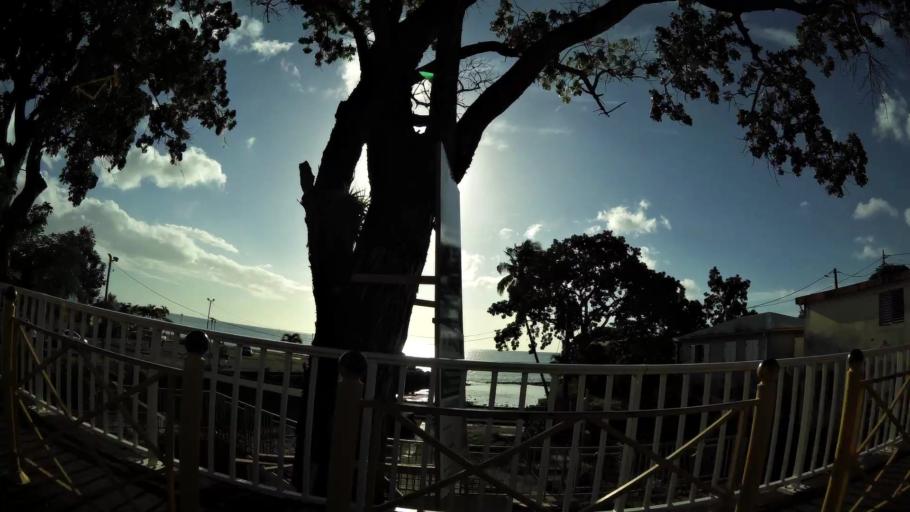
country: GP
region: Guadeloupe
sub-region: Guadeloupe
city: Pointe-Noire
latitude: 16.2321
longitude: -61.7896
